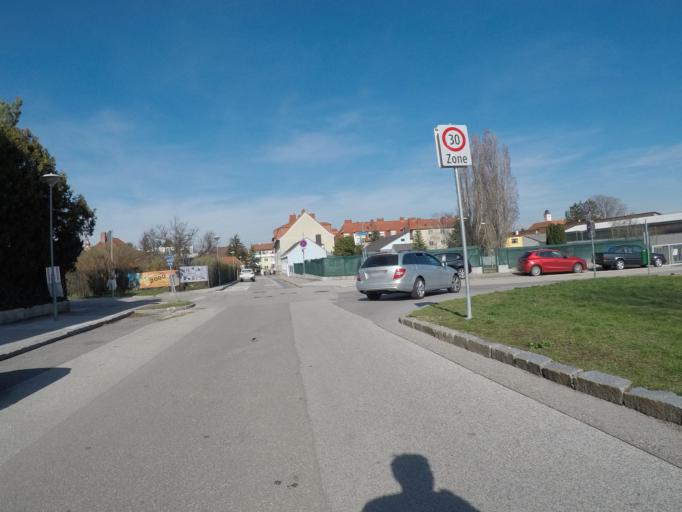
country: AT
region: Lower Austria
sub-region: Politischer Bezirk Modling
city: Vosendorf
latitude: 48.1193
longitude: 16.3389
